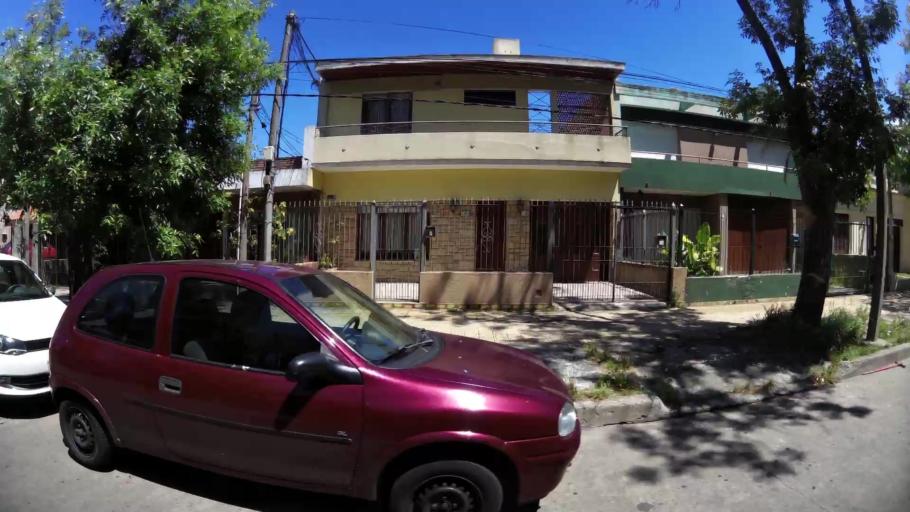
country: UY
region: Montevideo
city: Montevideo
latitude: -34.9008
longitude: -56.1300
